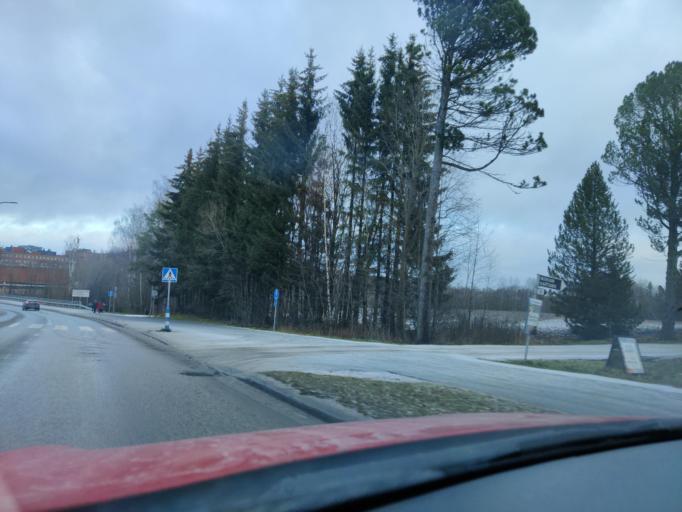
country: FI
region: Pirkanmaa
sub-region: Tampere
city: Nokia
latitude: 61.4709
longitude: 23.5047
